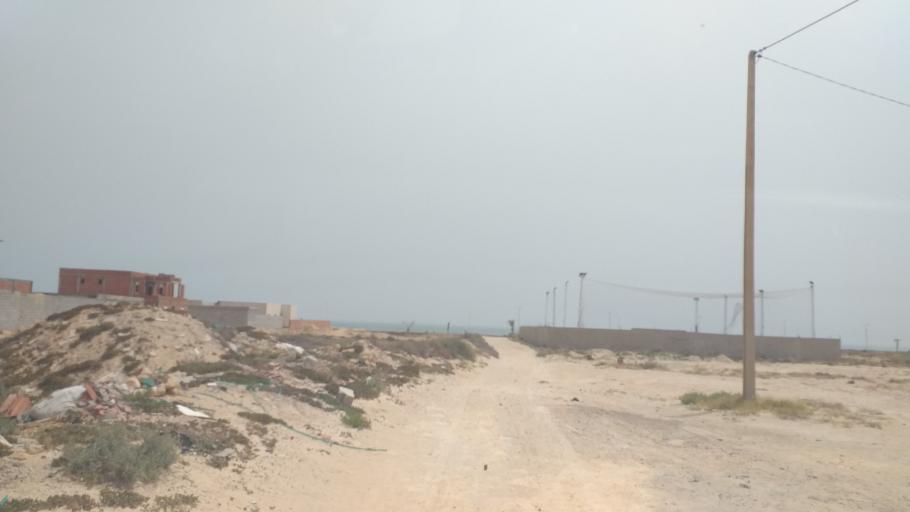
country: TN
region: Qabis
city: Gabes
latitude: 33.9562
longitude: 10.0664
